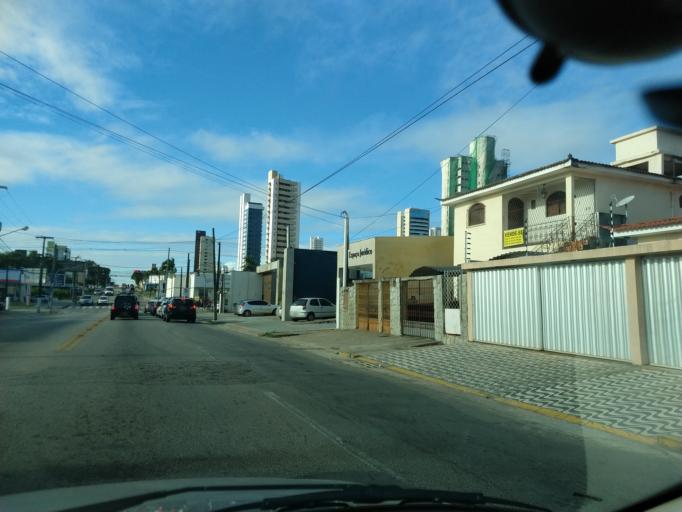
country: BR
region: Rio Grande do Norte
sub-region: Natal
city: Natal
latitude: -5.8225
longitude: -35.2196
